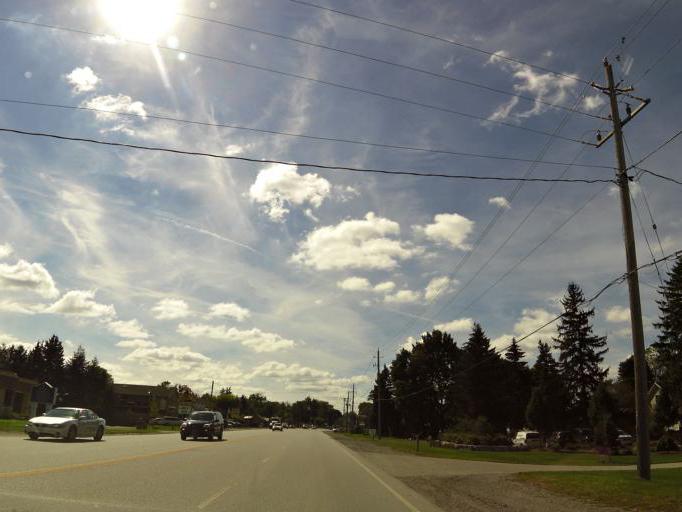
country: CA
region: Ontario
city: London
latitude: 42.9137
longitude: -81.2893
